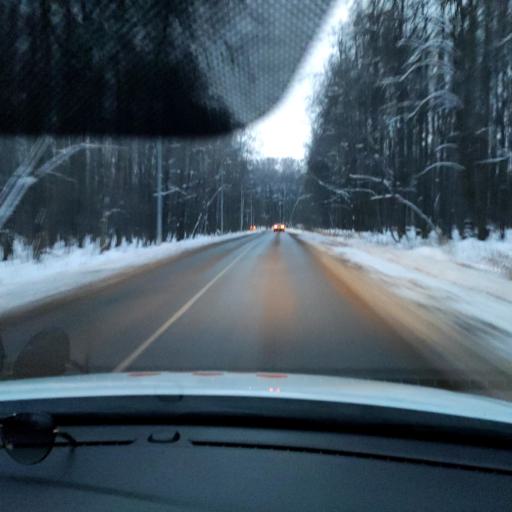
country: RU
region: Tatarstan
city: Vysokaya Gora
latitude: 55.9292
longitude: 49.1934
